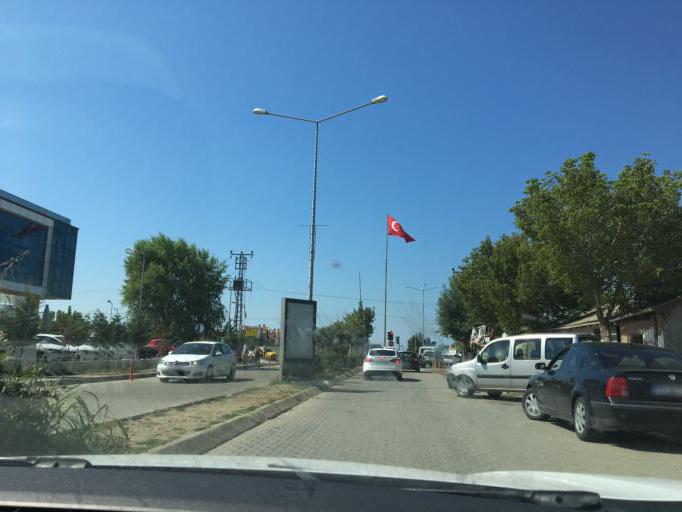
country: TR
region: Tekirdag
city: Marmara Ereglisi
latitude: 40.9948
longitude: 27.8423
